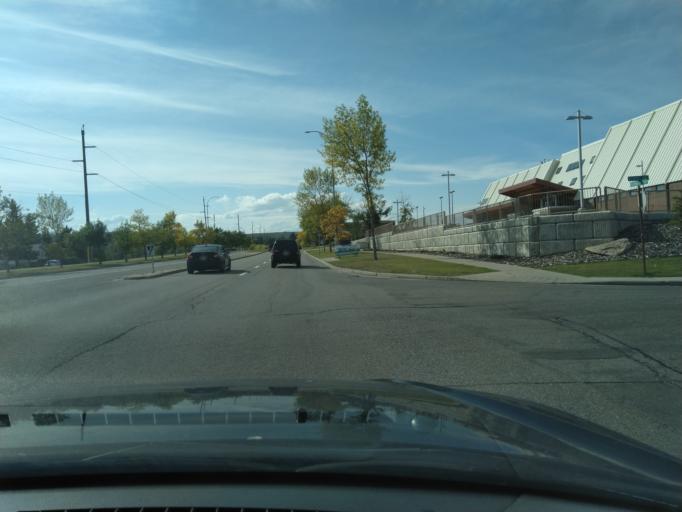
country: CA
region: Alberta
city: Calgary
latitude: 51.1253
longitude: -114.0665
